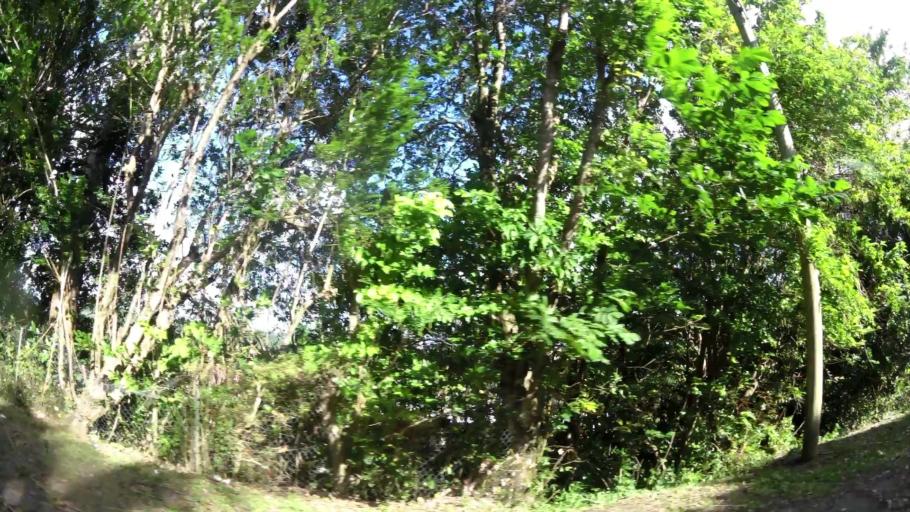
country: MQ
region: Martinique
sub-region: Martinique
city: Fort-de-France
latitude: 14.6361
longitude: -61.0719
